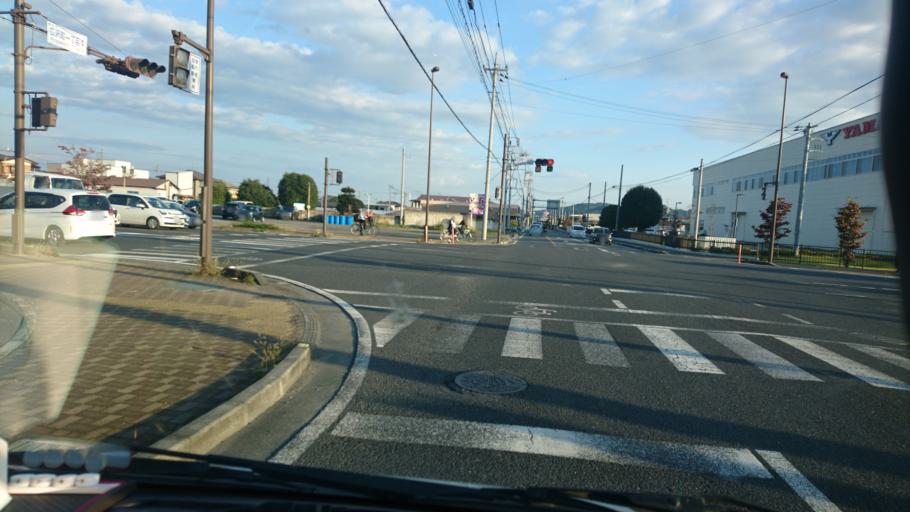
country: JP
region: Gunma
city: Kiryu
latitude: 36.3936
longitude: 139.3274
